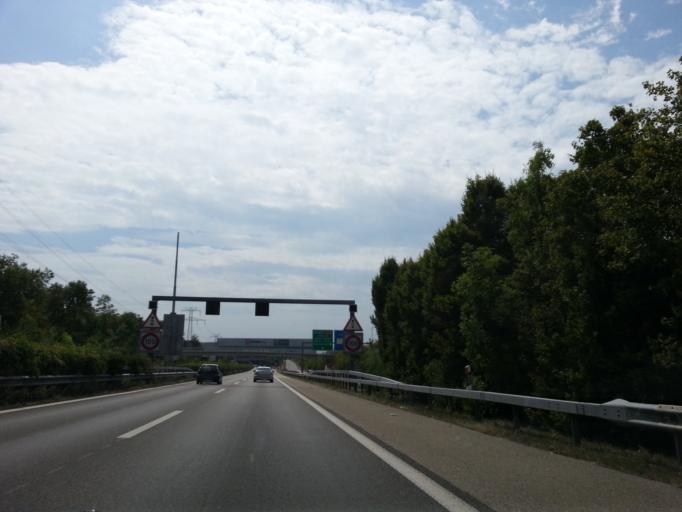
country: CH
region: Geneva
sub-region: Geneva
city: Le Grand-Saconnex
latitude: 46.2421
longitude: 6.1241
